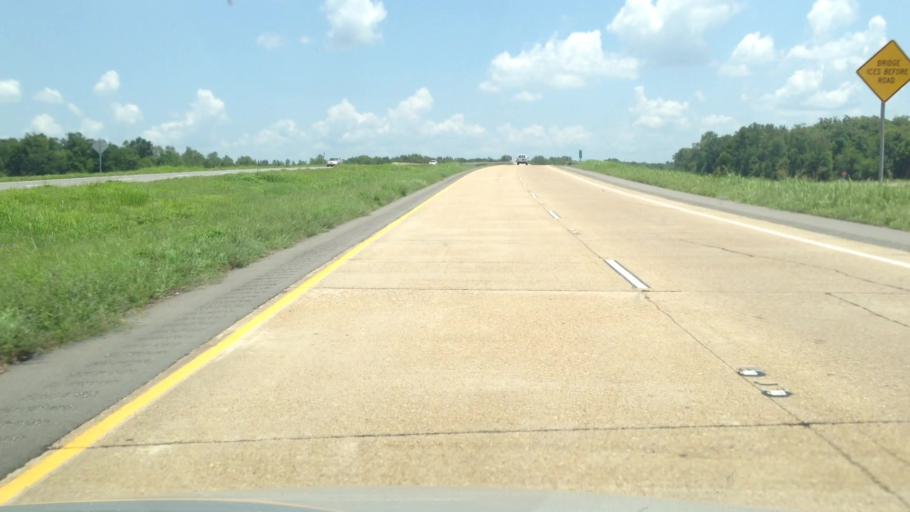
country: US
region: Louisiana
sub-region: Avoyelles Parish
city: Bunkie
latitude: 30.9887
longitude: -92.3108
